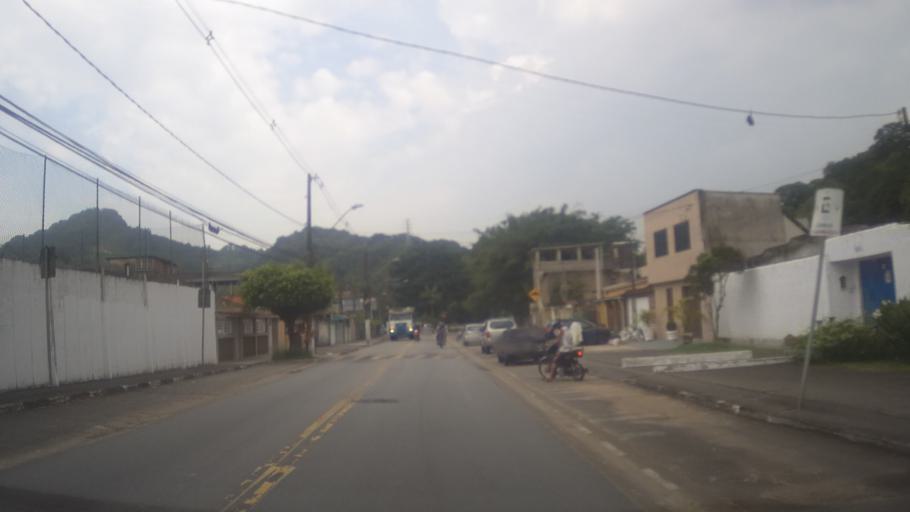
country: BR
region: Sao Paulo
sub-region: Santos
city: Santos
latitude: -23.9463
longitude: -46.3563
